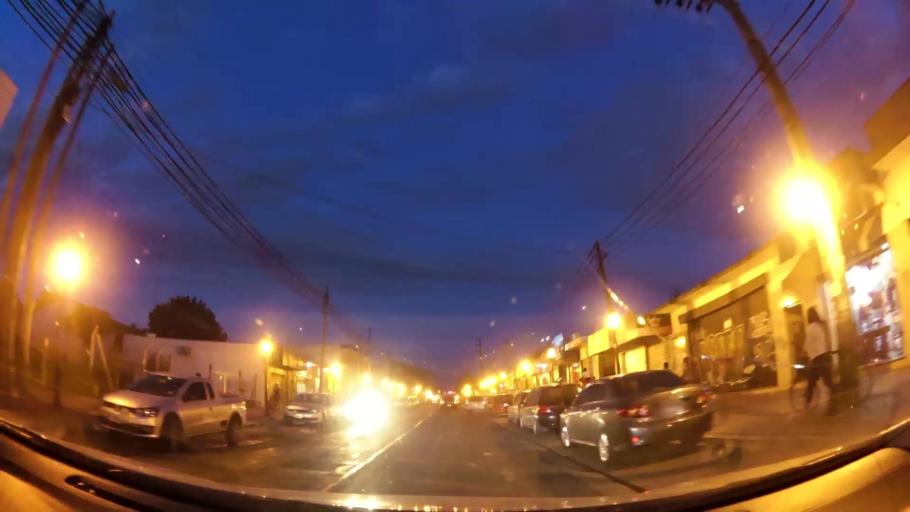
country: AR
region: Buenos Aires
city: Santa Catalina - Dique Lujan
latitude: -34.4134
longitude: -58.6920
